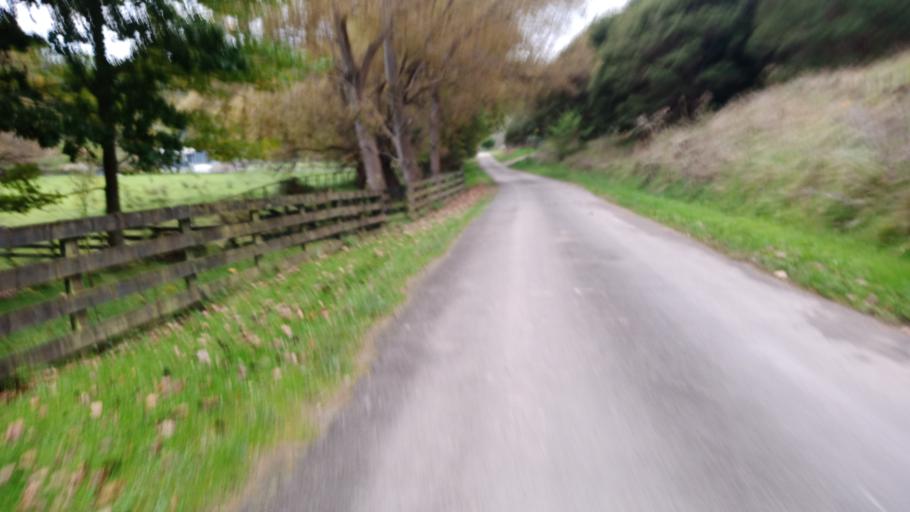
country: NZ
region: Gisborne
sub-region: Gisborne District
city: Gisborne
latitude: -38.6449
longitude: 178.0347
